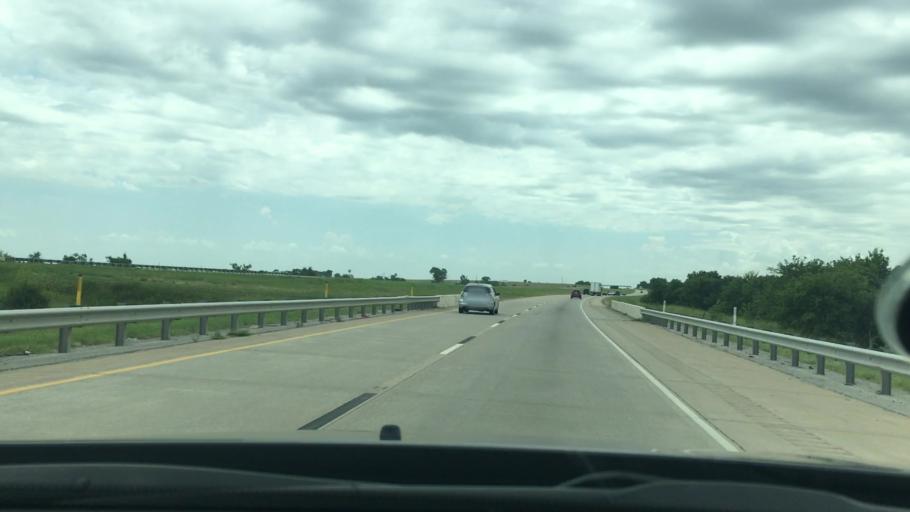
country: US
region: Oklahoma
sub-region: Love County
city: Marietta
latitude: 33.9773
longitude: -97.1349
